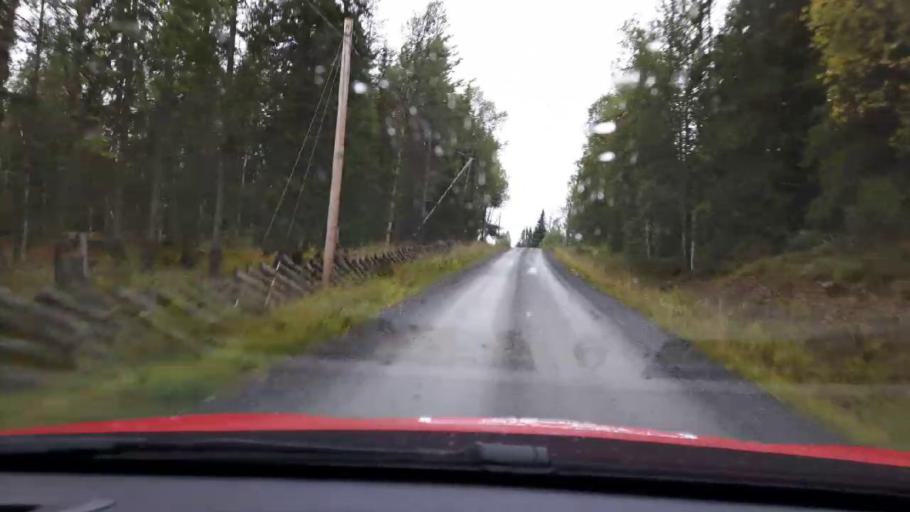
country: SE
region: Jaemtland
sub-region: Are Kommun
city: Are
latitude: 63.5128
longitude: 12.7179
